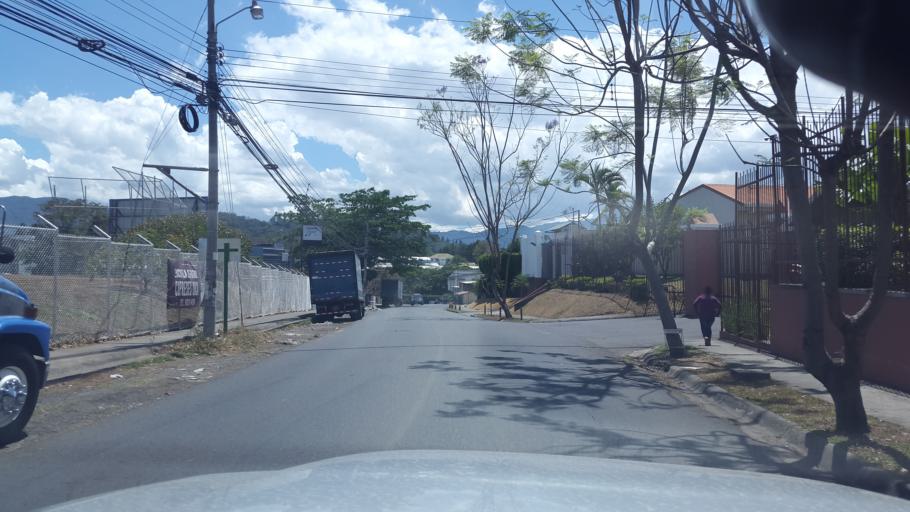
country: CR
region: San Jose
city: Curridabat
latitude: 9.9174
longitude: -84.0268
